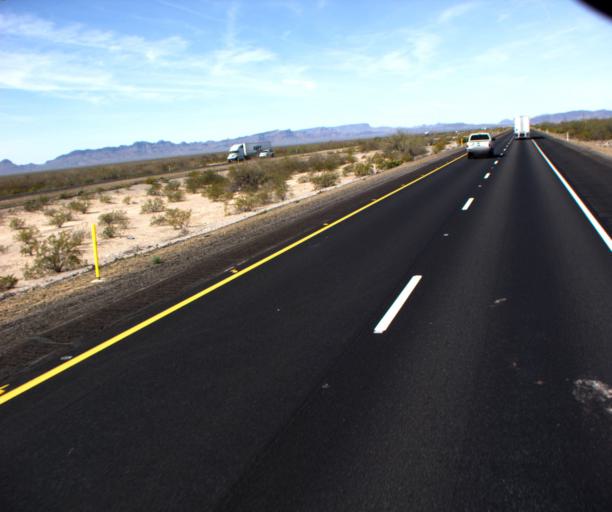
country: US
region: Arizona
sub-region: La Paz County
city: Salome
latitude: 33.6229
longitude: -113.7108
